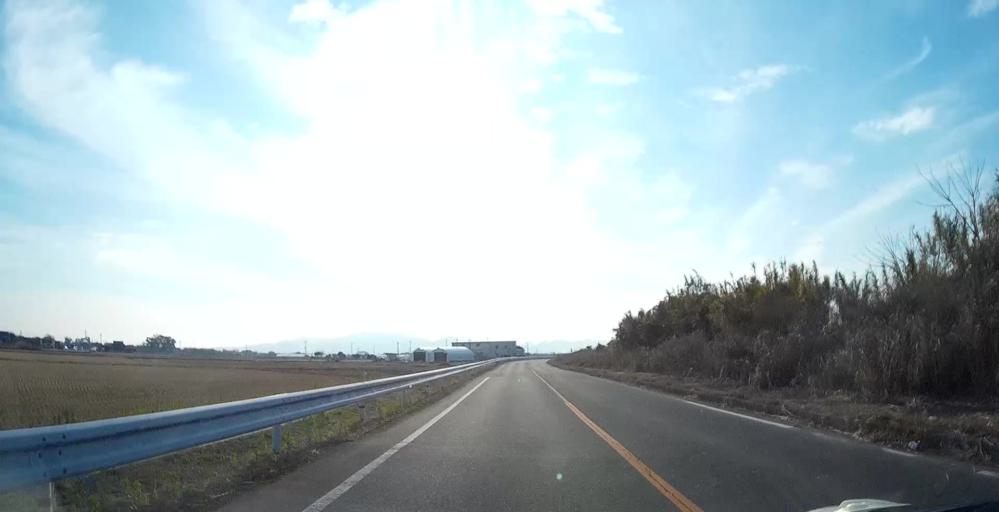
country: JP
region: Kumamoto
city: Uto
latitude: 32.7421
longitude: 130.6717
